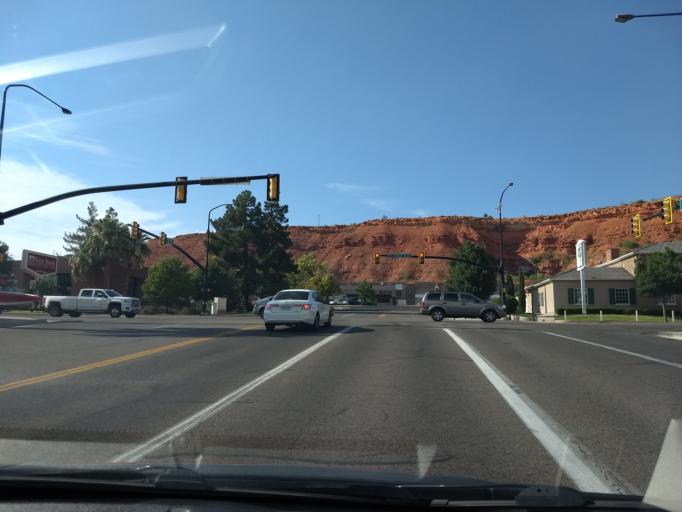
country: US
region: Utah
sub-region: Washington County
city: Saint George
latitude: 37.1095
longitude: -113.5748
